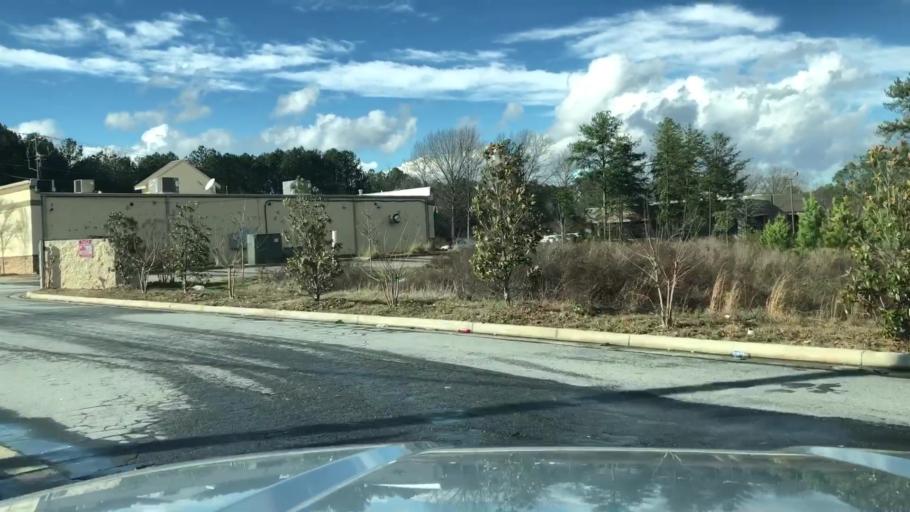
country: US
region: Georgia
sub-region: Fulton County
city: College Park
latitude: 33.6083
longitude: -84.4453
